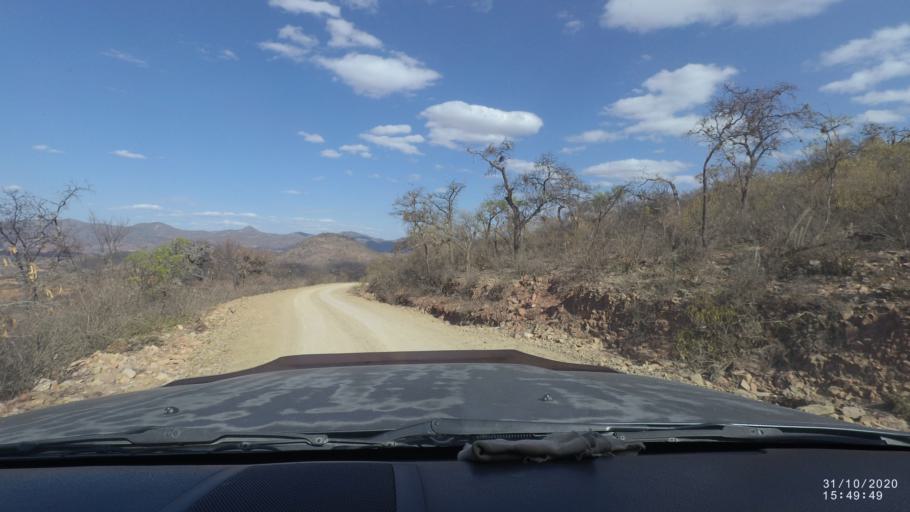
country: BO
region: Chuquisaca
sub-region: Provincia Zudanez
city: Mojocoya
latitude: -18.3133
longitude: -64.7071
